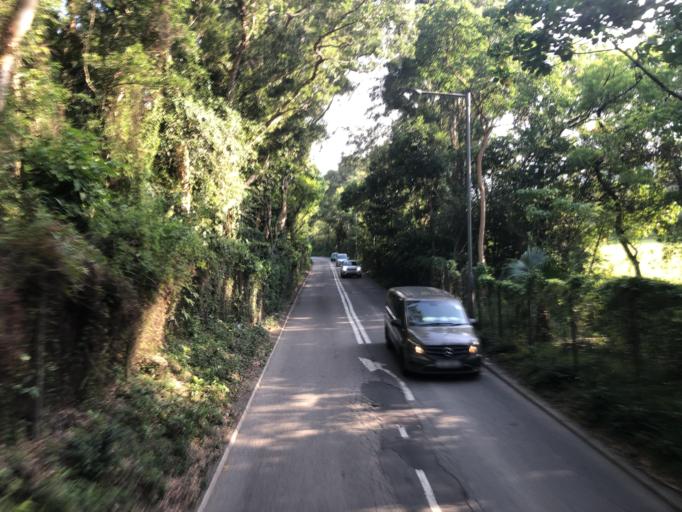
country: HK
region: Tai Po
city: Tai Po
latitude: 22.4896
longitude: 114.1169
